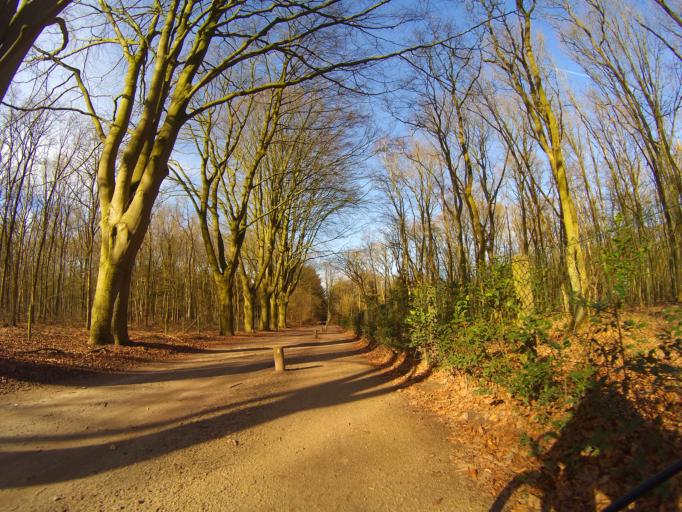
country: NL
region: North Holland
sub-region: Gemeente Huizen
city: Huizen
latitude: 52.3065
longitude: 5.2099
